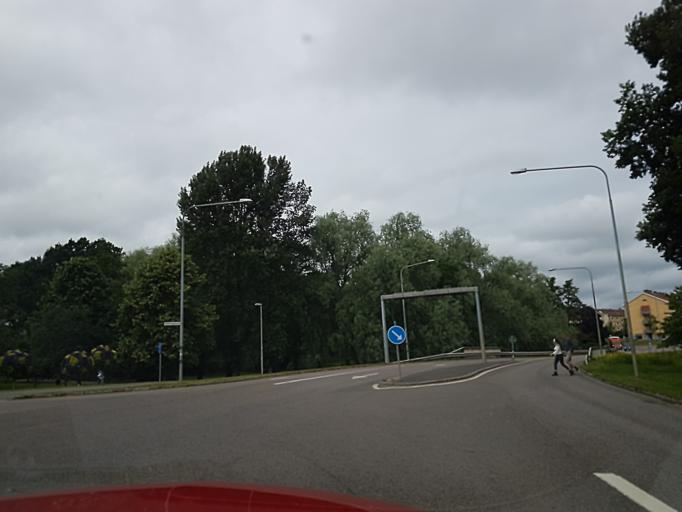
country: SE
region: Vaestra Goetaland
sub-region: Skovde Kommun
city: Skoevde
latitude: 58.3932
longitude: 13.8477
